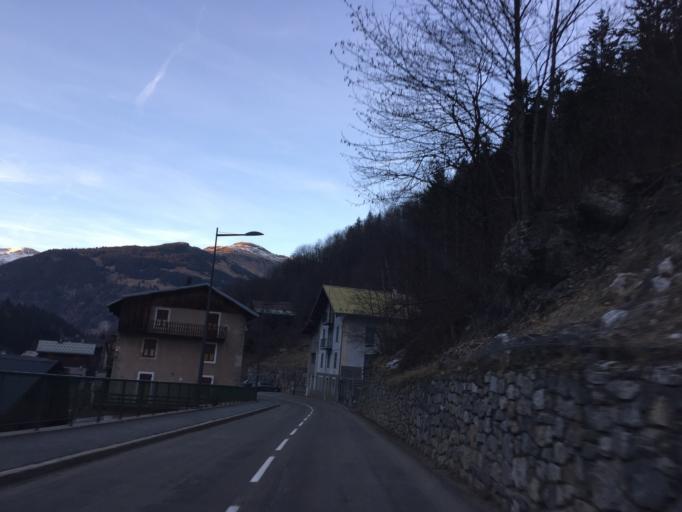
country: FR
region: Rhone-Alpes
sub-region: Departement de la Savoie
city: Bozel
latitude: 45.4247
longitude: 6.6977
